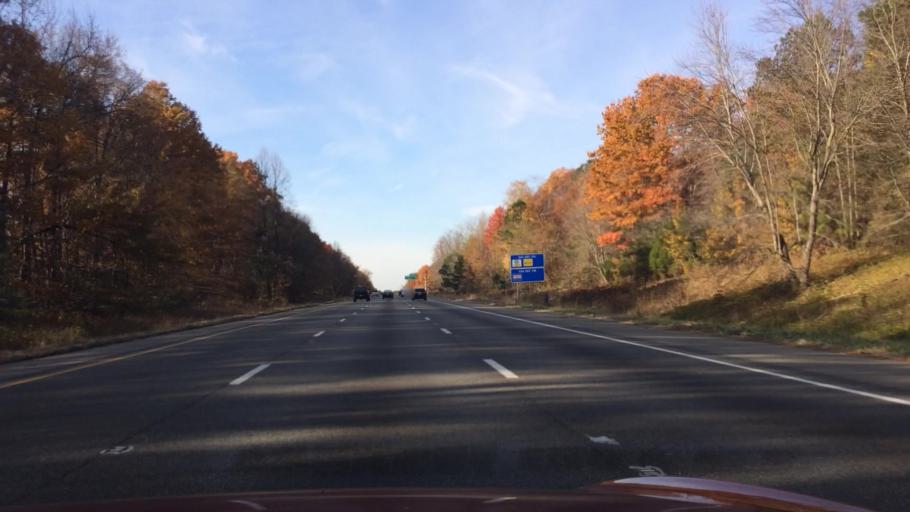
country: US
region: Virginia
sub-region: Henrico County
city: Wyndham
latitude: 37.6747
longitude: -77.5695
